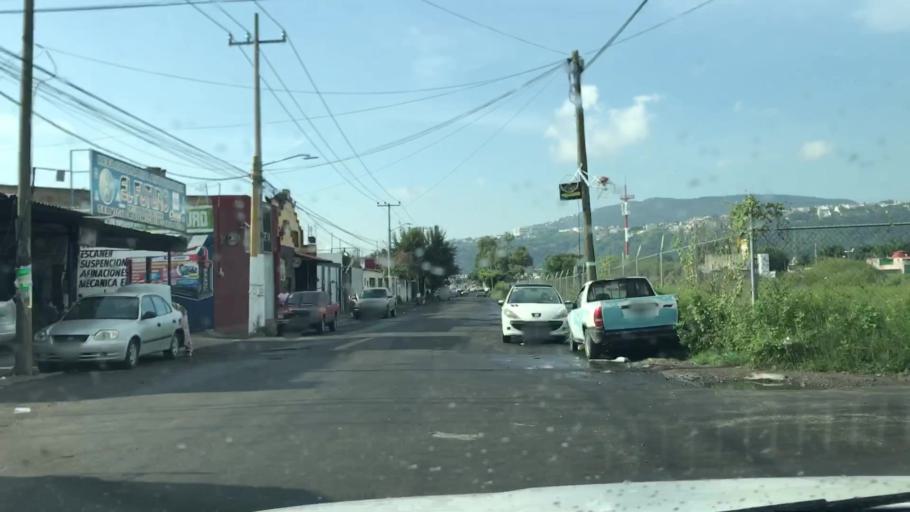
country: MX
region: Jalisco
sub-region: Tlajomulco de Zuniga
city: Palomar
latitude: 20.6330
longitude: -103.4544
